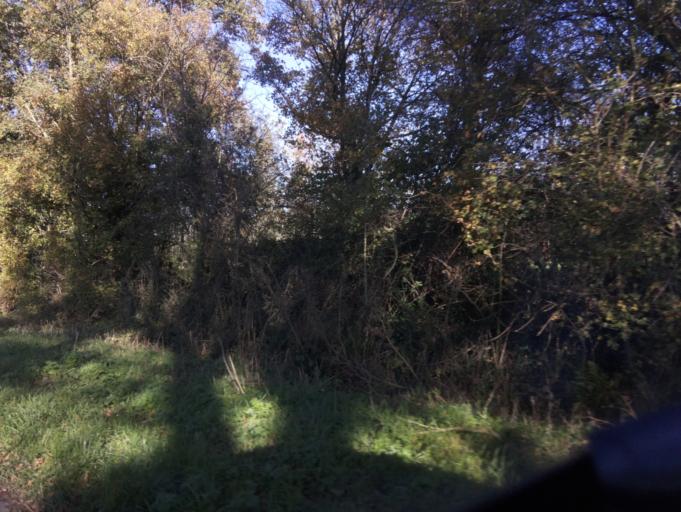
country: GB
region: England
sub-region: Dorset
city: Sherborne
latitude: 50.8699
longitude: -2.5248
